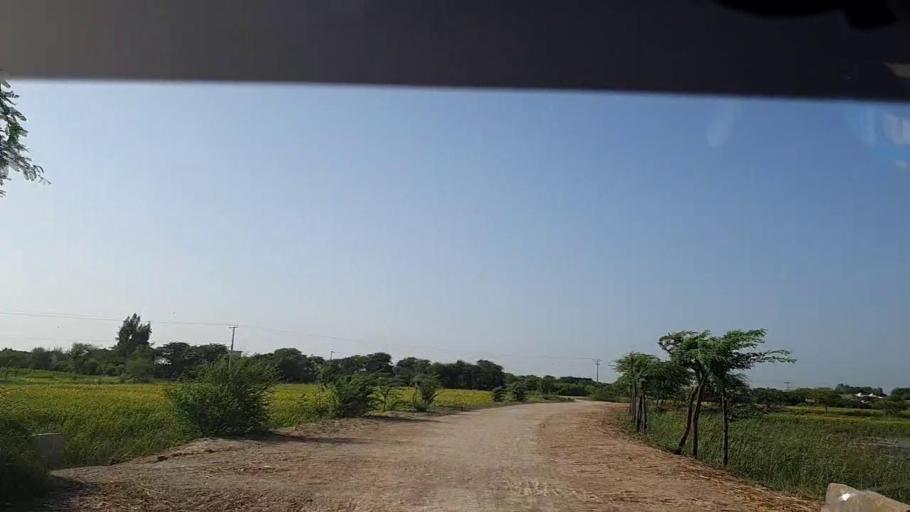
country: PK
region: Sindh
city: Badin
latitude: 24.6881
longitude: 68.8411
